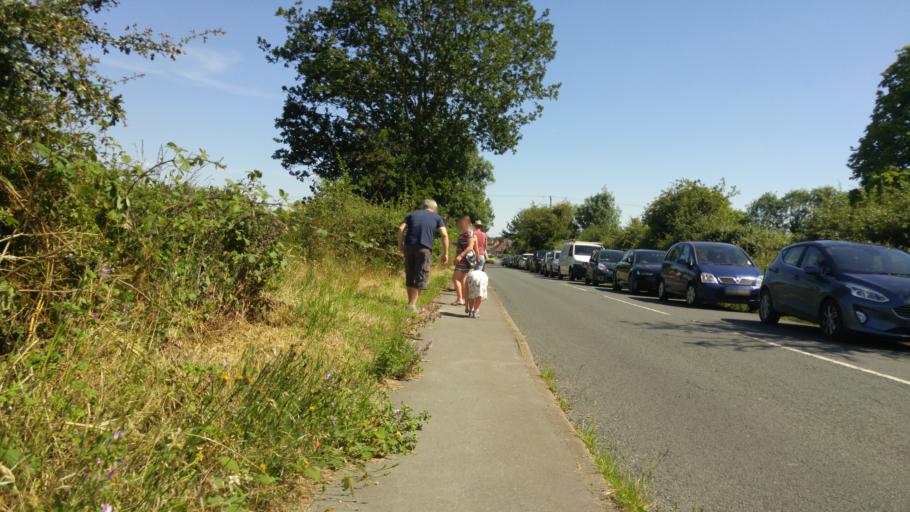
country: GB
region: England
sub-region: Essex
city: Rowhedge
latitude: 51.8606
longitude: 0.9403
